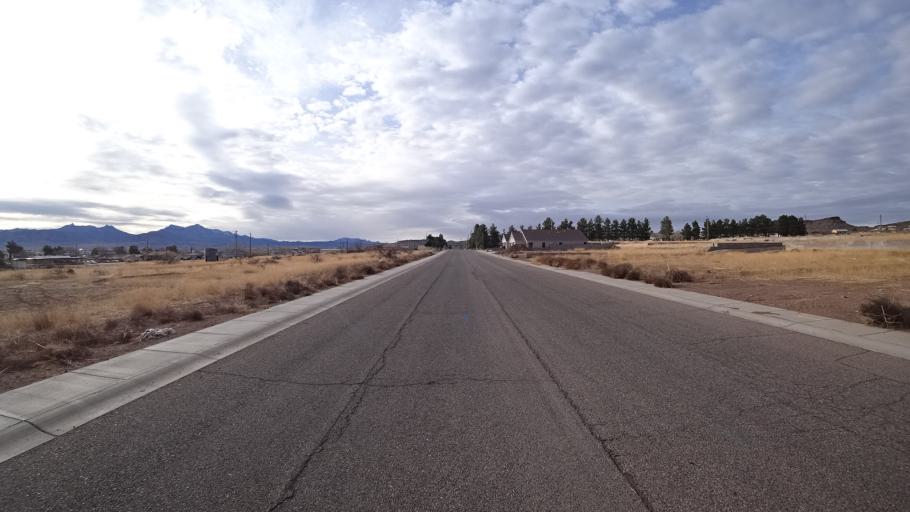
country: US
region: Arizona
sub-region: Mohave County
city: Kingman
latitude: 35.2235
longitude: -114.0446
